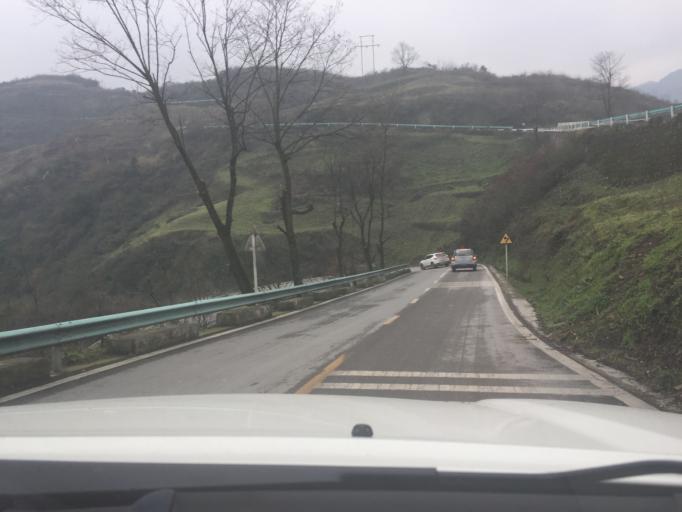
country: CN
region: Guizhou Sheng
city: Supu
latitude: 27.1015
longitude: 106.8138
